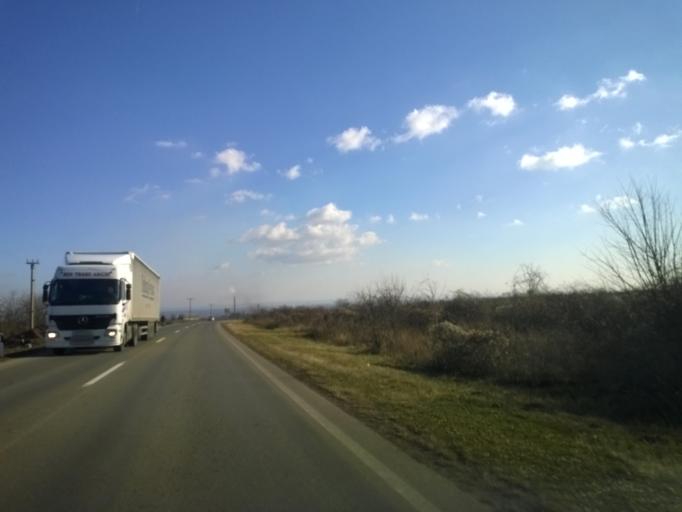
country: RS
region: Central Serbia
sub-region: Podunavski Okrug
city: Smederevo
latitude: 44.6121
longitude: 20.9281
